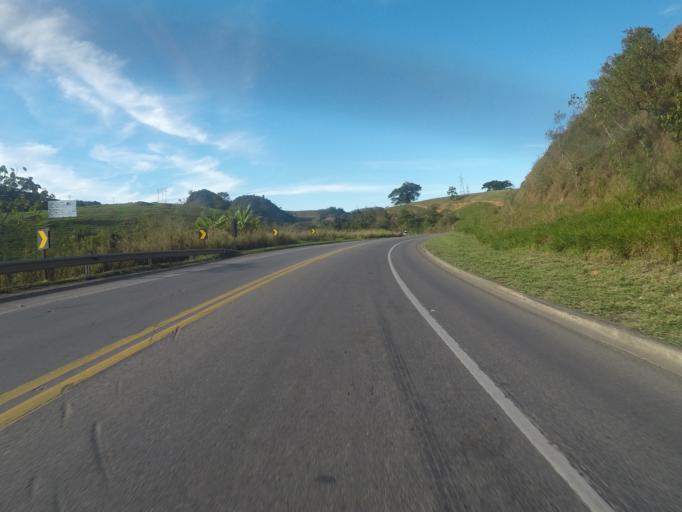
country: BR
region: Espirito Santo
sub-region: Ibiracu
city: Ibiracu
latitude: -19.8708
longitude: -40.4113
